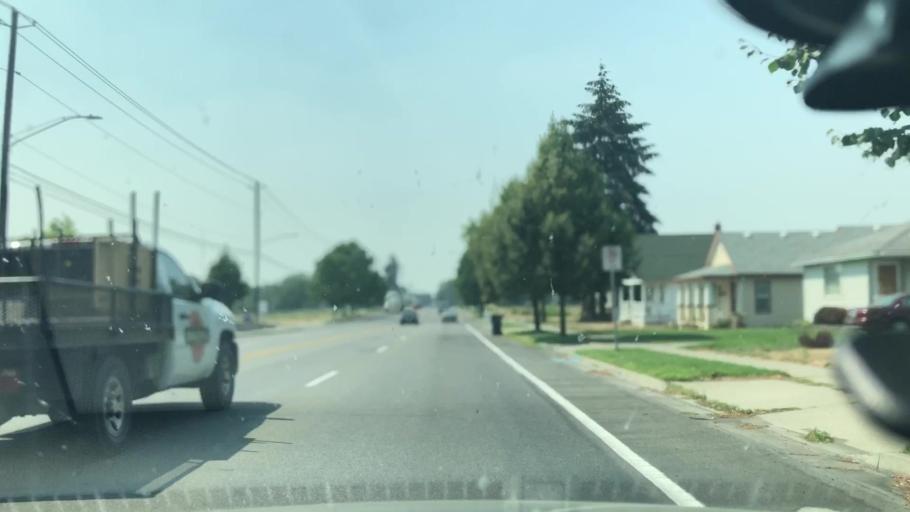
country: US
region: Washington
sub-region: Spokane County
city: Spokane
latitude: 47.6863
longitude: -117.3610
